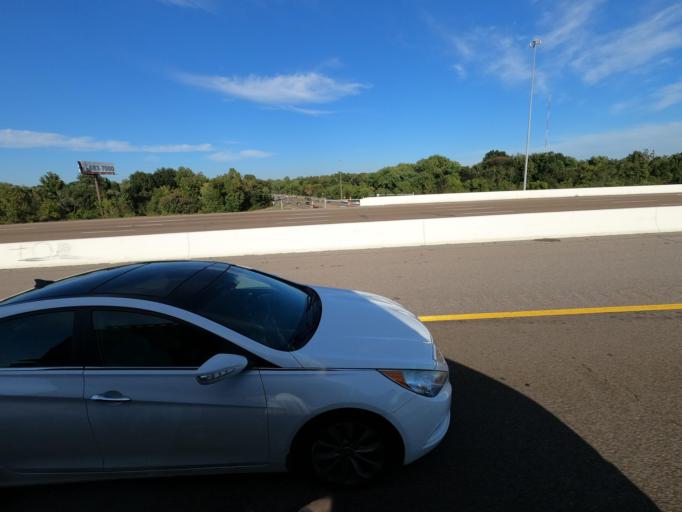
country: US
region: Tennessee
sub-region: Shelby County
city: Bartlett
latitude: 35.1692
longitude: -89.9026
